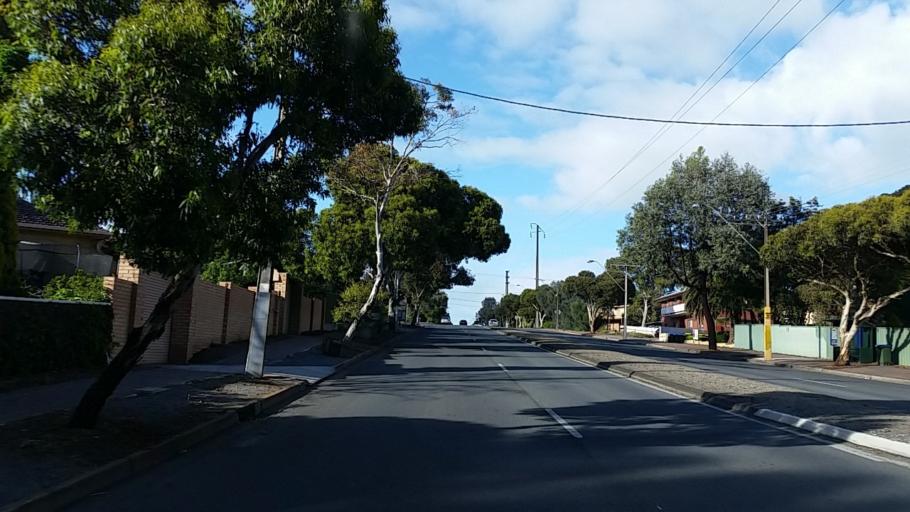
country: AU
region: South Australia
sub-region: Mitcham
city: Clapham
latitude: -35.0035
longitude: 138.5894
